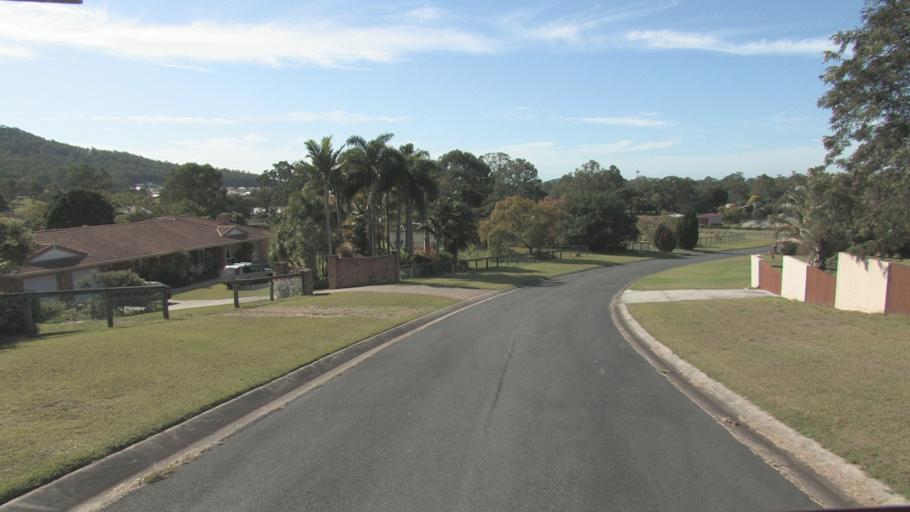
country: AU
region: Queensland
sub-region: Logan
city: Windaroo
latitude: -27.7596
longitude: 153.1801
